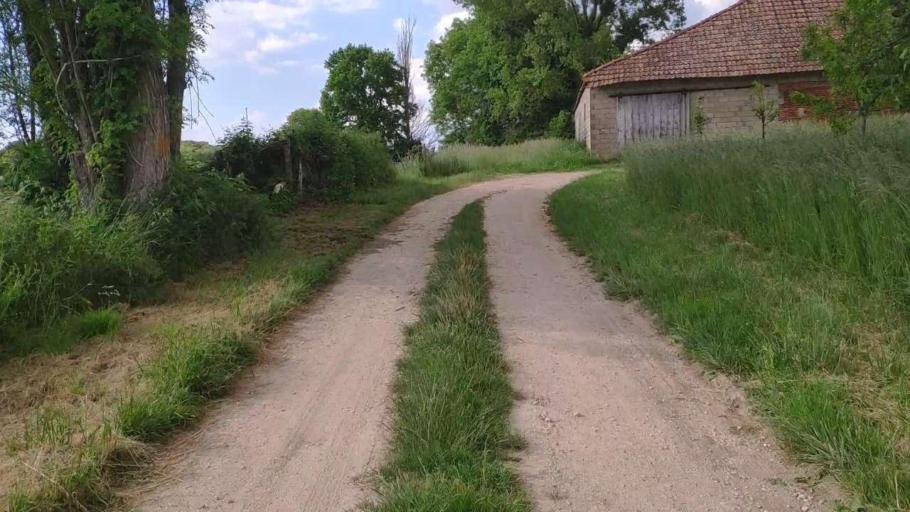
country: FR
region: Bourgogne
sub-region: Departement de Saone-et-Loire
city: Saint-Germain-du-Bois
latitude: 46.8054
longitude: 5.3444
